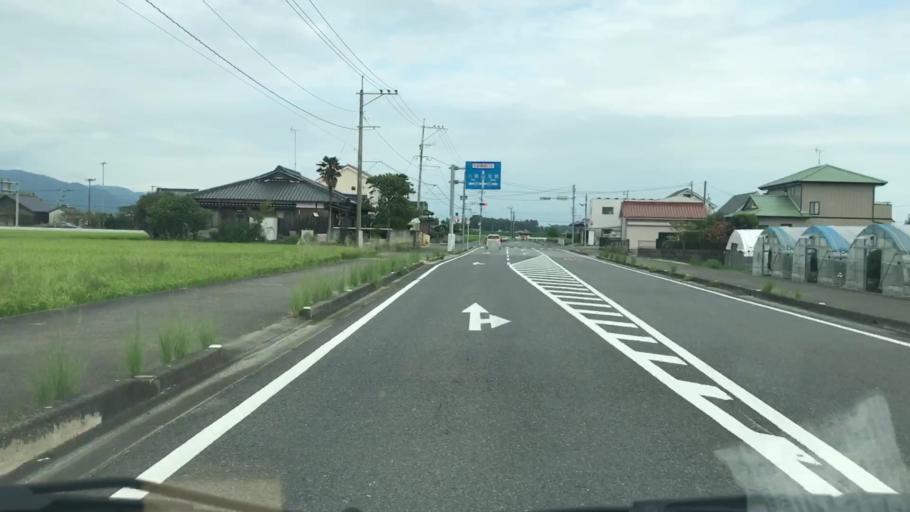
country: JP
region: Saga Prefecture
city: Saga-shi
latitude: 33.2918
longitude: 130.2384
